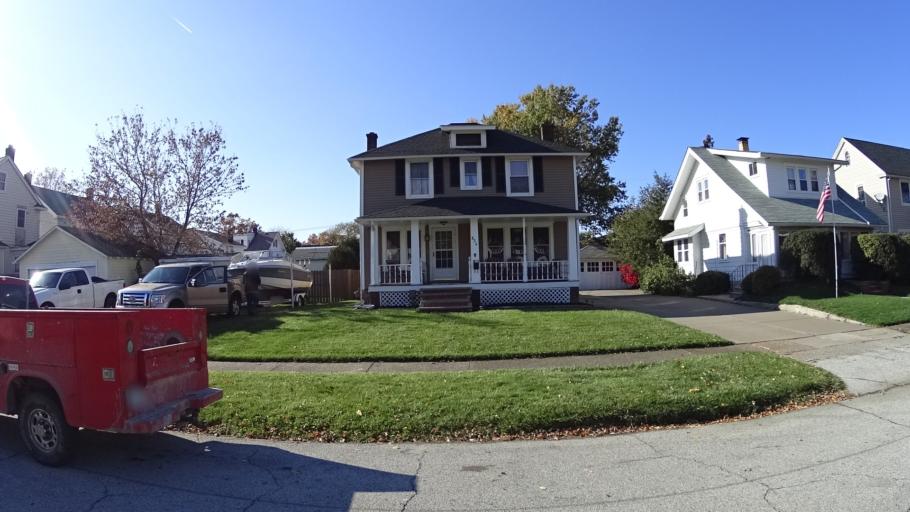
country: US
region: Ohio
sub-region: Lorain County
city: Lorain
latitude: 41.4610
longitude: -82.1898
